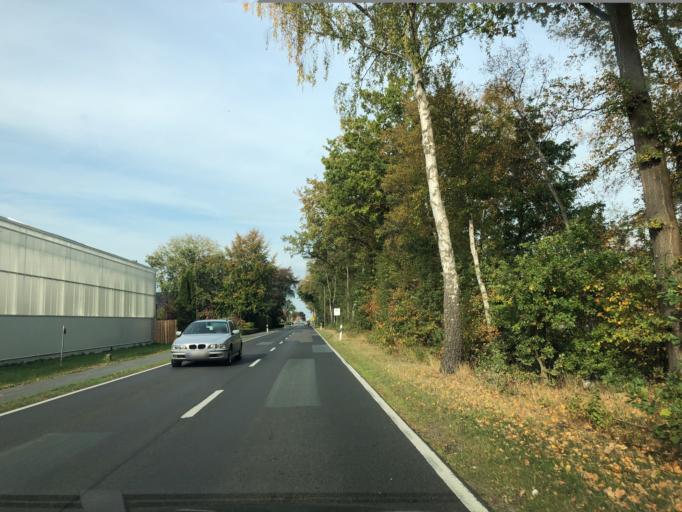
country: DE
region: Lower Saxony
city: Papenburg
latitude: 53.0385
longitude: 7.4688
